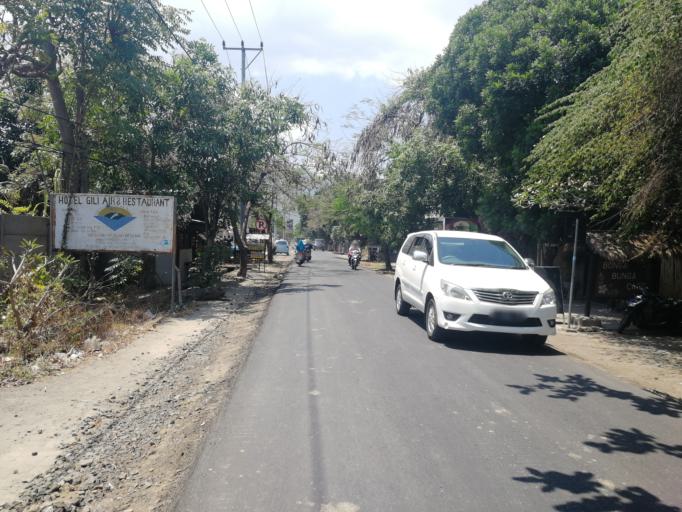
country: ID
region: West Nusa Tenggara
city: Pemenang
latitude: -8.3985
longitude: 116.1008
